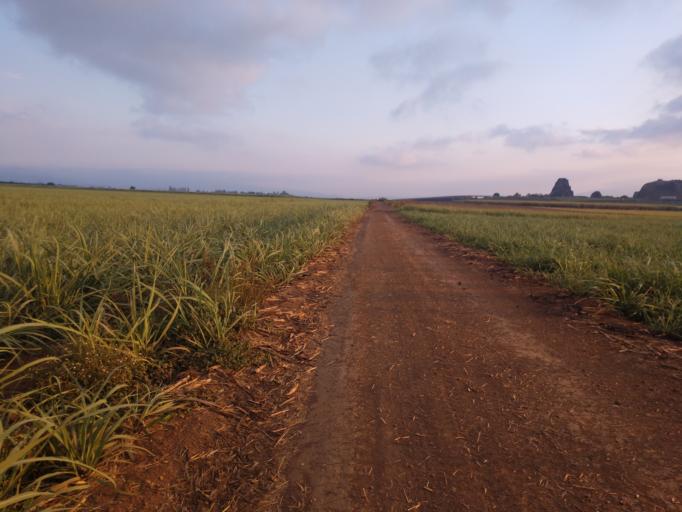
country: MX
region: Nayarit
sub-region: Tepic
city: La Corregidora
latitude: 21.4824
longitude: -104.8051
